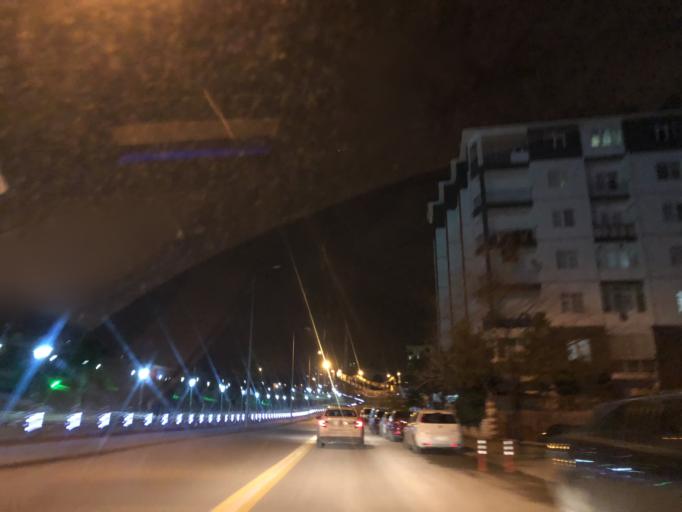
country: TR
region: Ankara
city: Batikent
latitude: 39.9673
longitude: 32.7802
